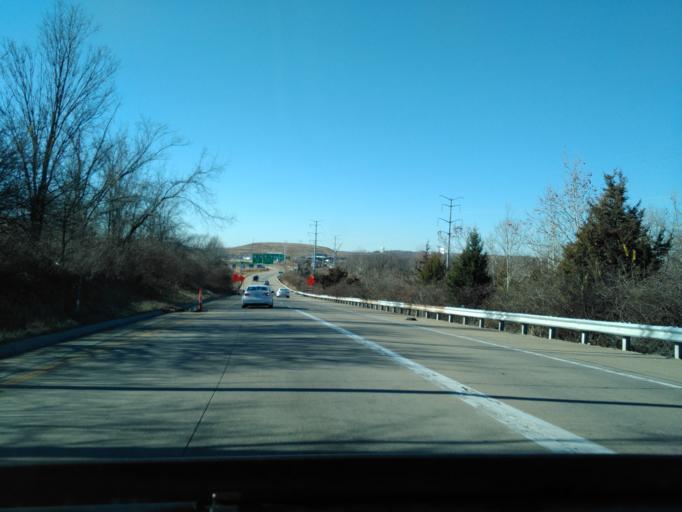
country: US
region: Missouri
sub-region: Saint Louis County
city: Valley Park
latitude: 38.5398
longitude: -90.4865
